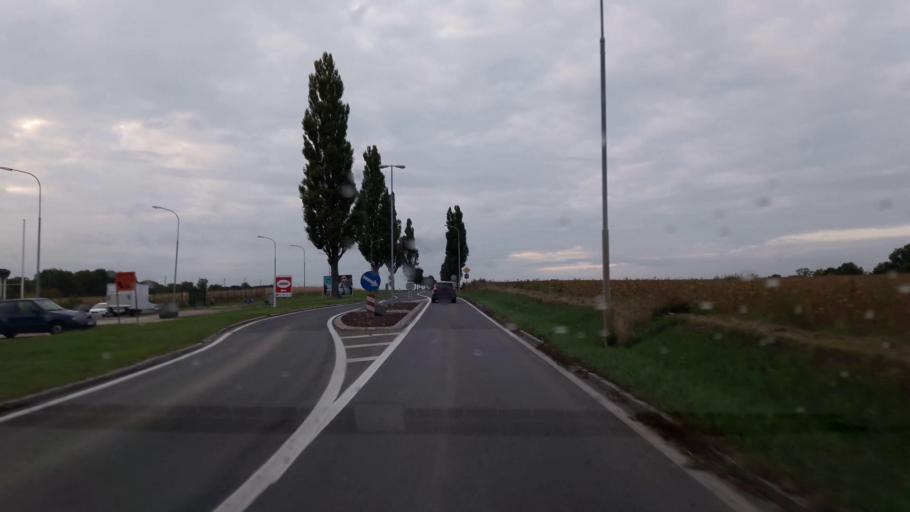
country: AT
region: Lower Austria
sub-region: Politischer Bezirk Wien-Umgebung
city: Schwadorf
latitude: 48.0757
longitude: 16.5761
